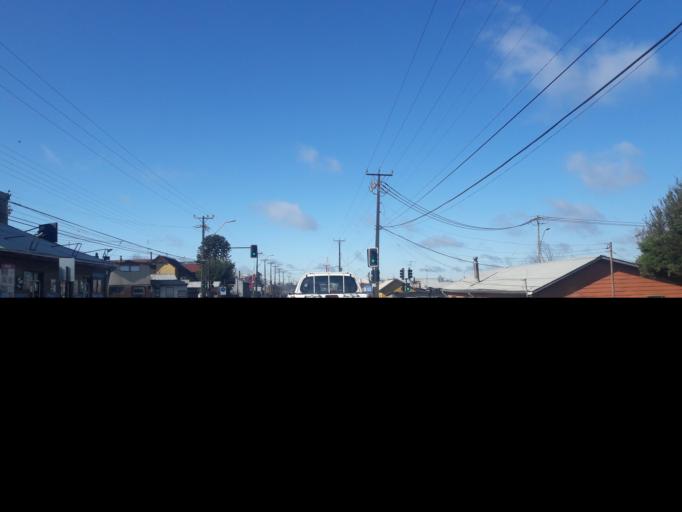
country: CL
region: Araucania
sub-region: Provincia de Malleco
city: Victoria
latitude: -38.2414
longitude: -72.3258
